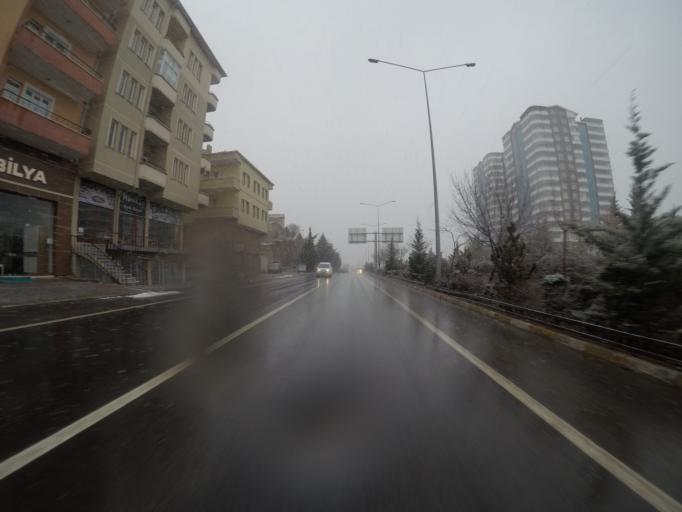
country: TR
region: Nevsehir
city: Nevsehir
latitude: 38.6306
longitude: 34.7327
